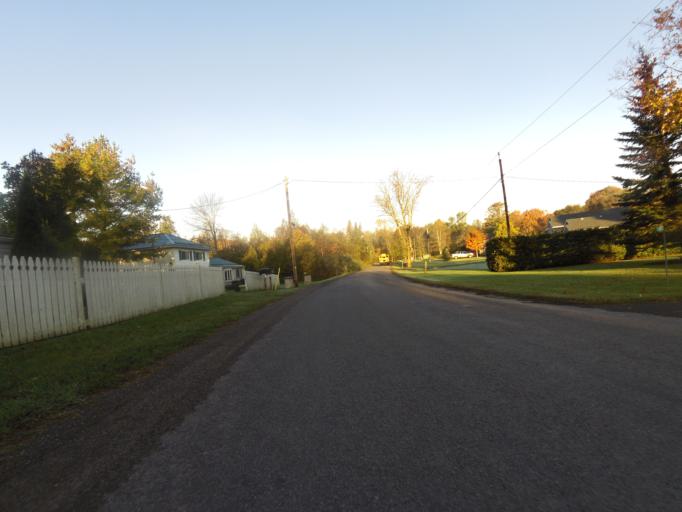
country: CA
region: Ontario
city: Quinte West
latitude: 44.0320
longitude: -77.5729
